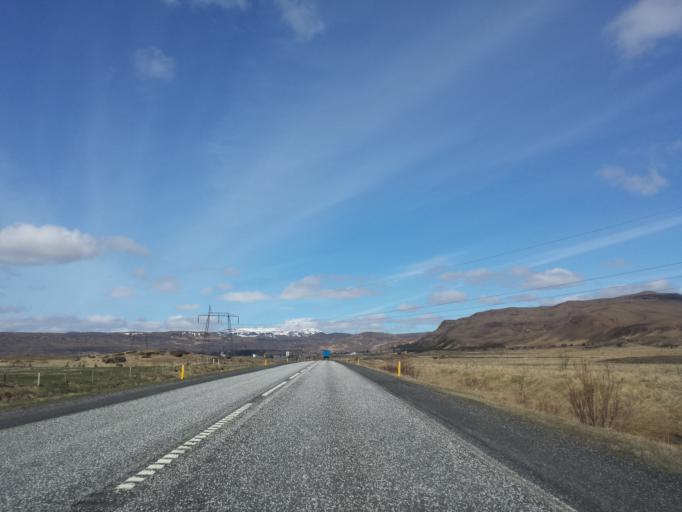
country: IS
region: South
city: Hveragerdi
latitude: 63.9806
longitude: -21.1528
